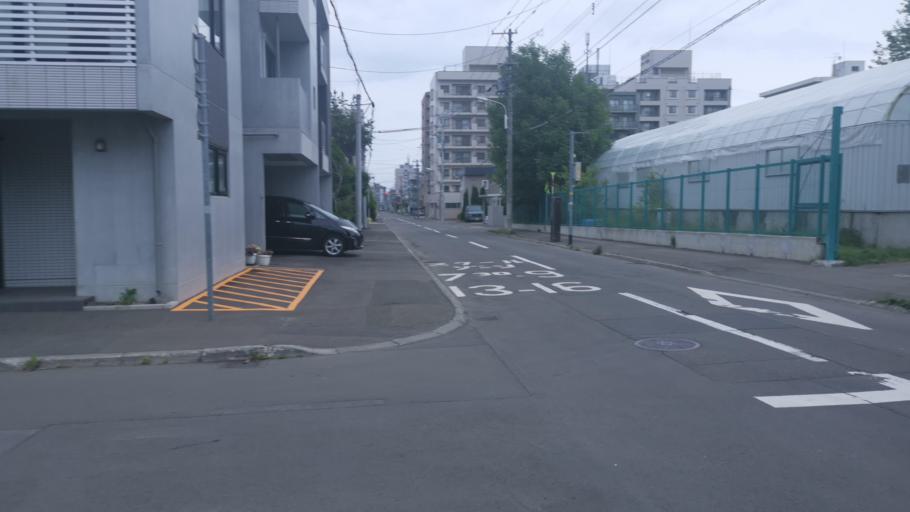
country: JP
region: Hokkaido
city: Sapporo
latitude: 43.0462
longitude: 141.3306
